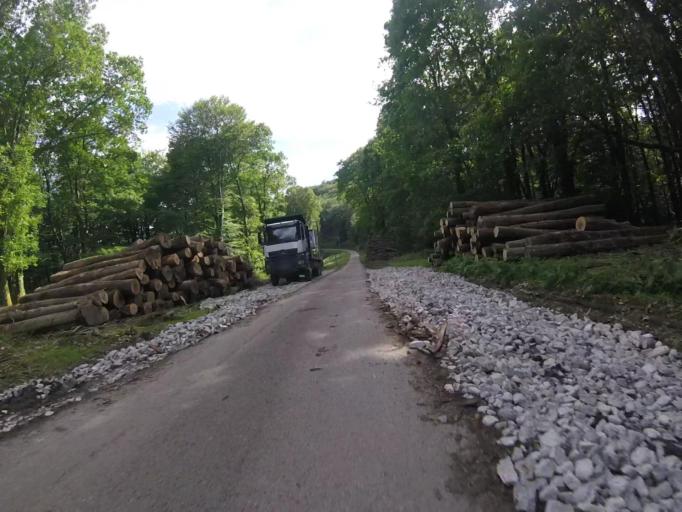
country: ES
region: Navarre
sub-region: Provincia de Navarra
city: Goizueta
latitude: 43.2360
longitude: -1.8043
